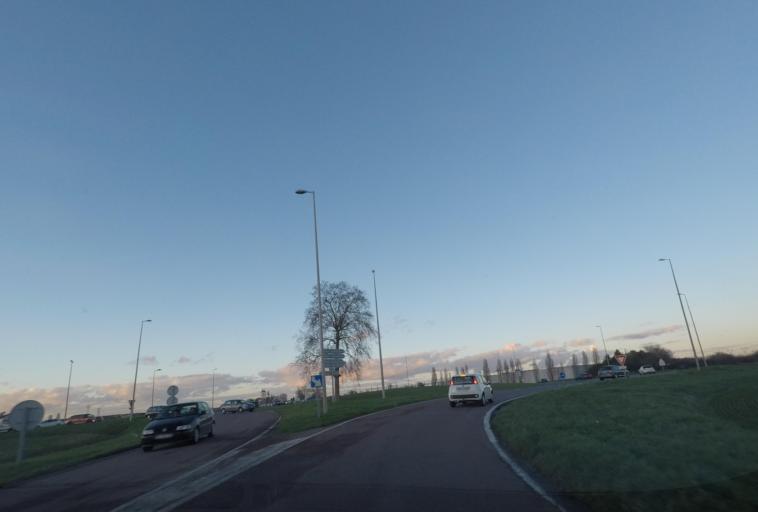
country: FR
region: Ile-de-France
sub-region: Departement de l'Essonne
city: Lisses
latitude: 48.5888
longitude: 2.4311
